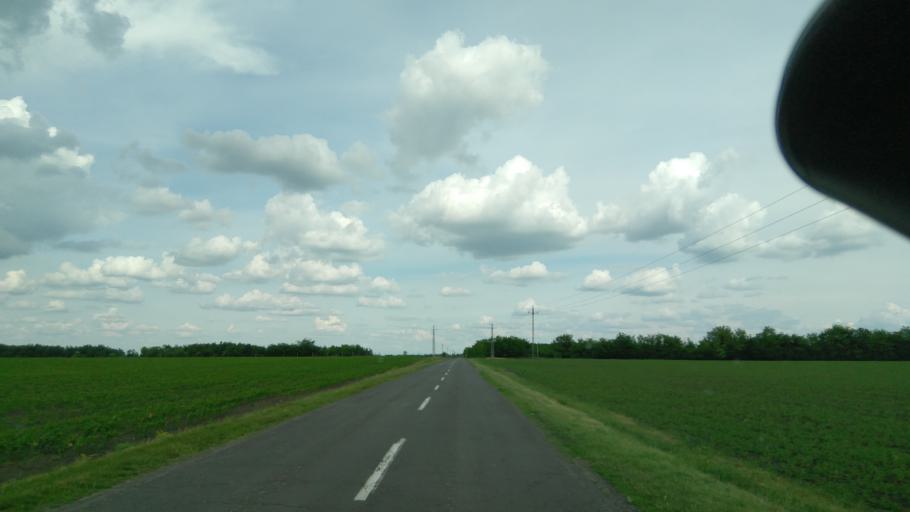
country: RO
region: Arad
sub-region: Comuna Peregu Mare
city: Peregu Mic
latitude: 46.3019
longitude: 20.9235
